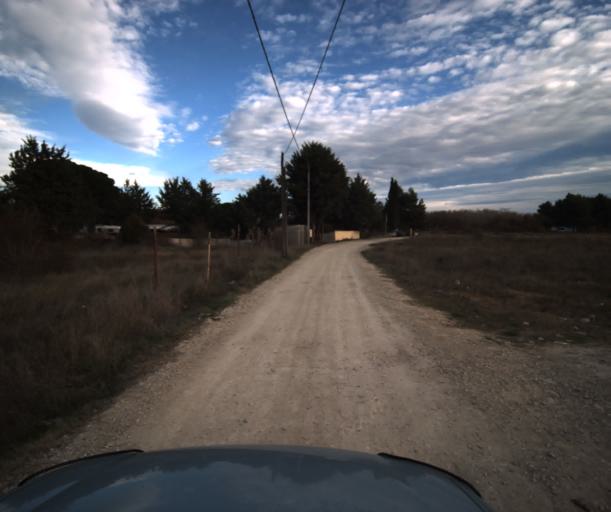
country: FR
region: Provence-Alpes-Cote d'Azur
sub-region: Departement des Bouches-du-Rhone
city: Meyrargues
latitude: 43.6645
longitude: 5.5283
